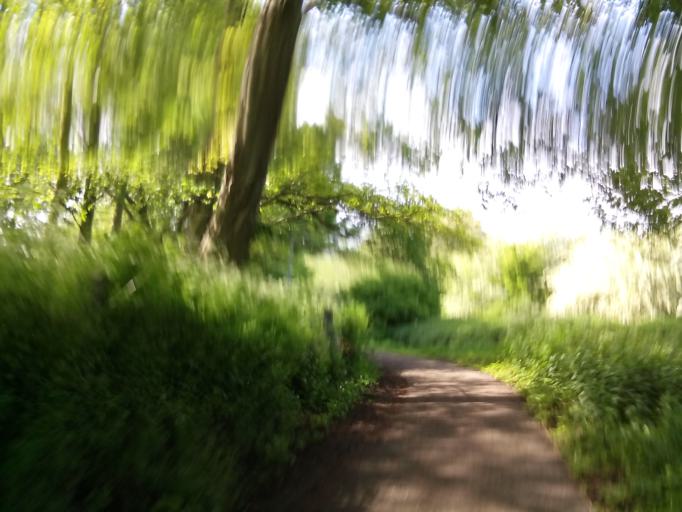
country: GB
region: England
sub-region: Cambridgeshire
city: Cambridge
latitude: 52.1909
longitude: 0.1652
